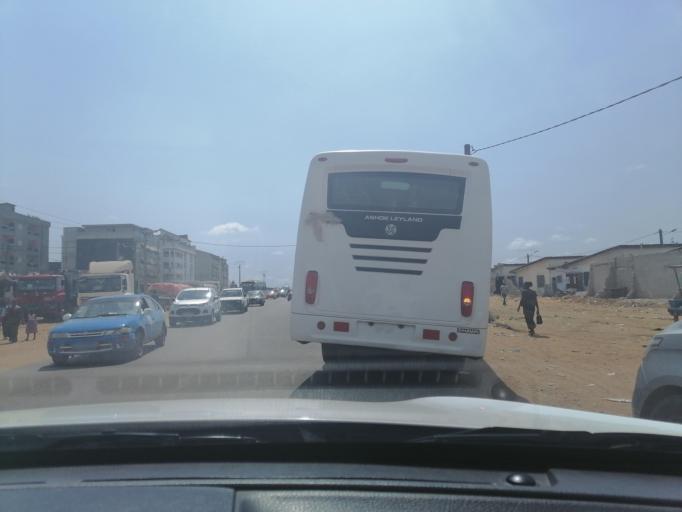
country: CI
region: Lagunes
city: Abidjan
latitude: 5.3497
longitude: -4.1046
